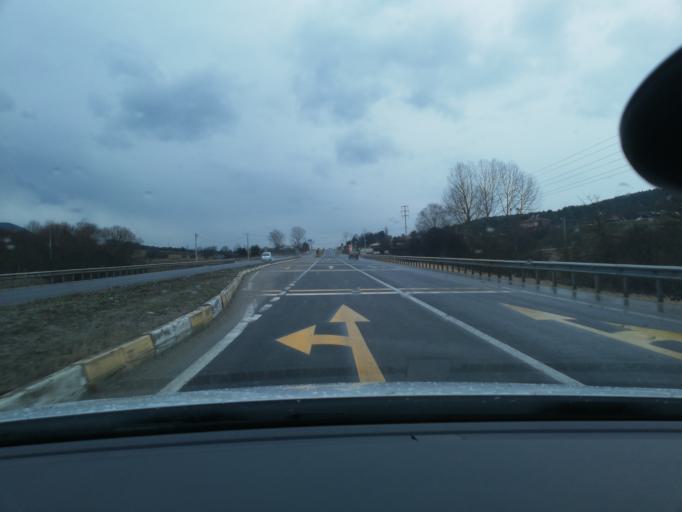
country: TR
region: Bolu
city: Yenicaga
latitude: 40.7584
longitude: 31.9301
